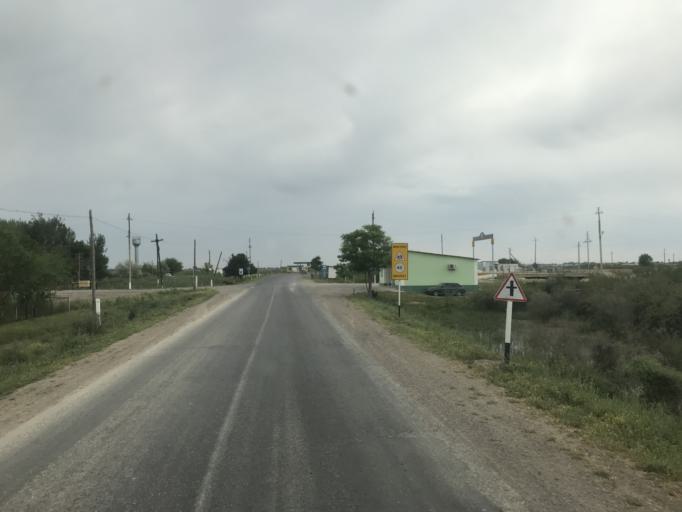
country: KZ
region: Ongtustik Qazaqstan
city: Asykata
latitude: 40.9119
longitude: 68.3933
